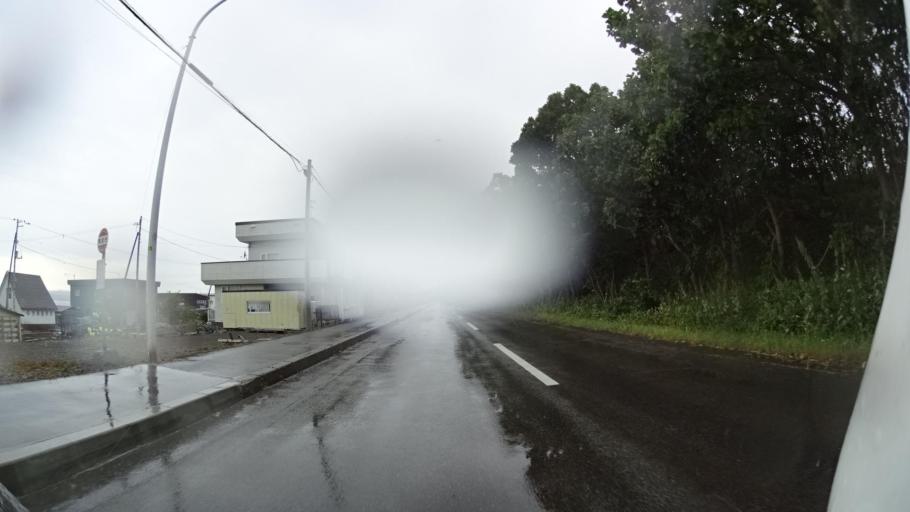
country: JP
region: Hokkaido
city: Mombetsu
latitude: 44.3319
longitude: 143.4908
